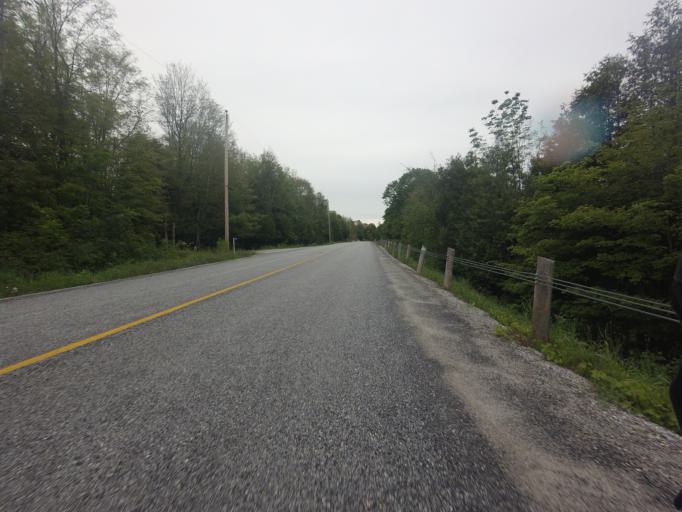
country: CA
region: Ontario
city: Perth
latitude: 44.9028
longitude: -76.4933
